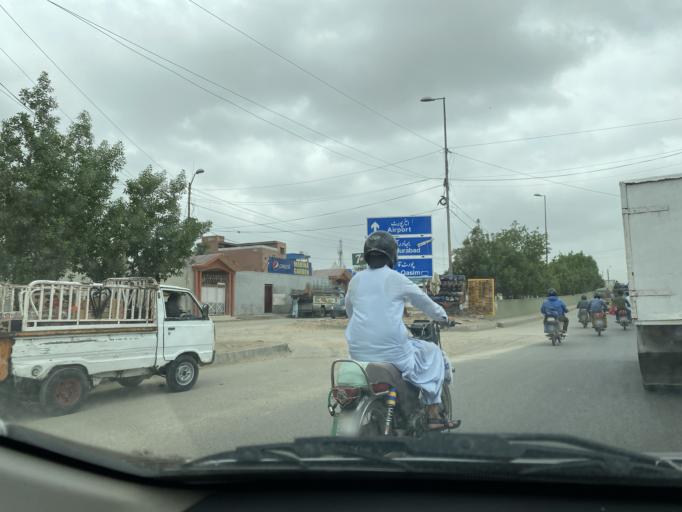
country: PK
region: Sindh
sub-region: Karachi District
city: Karachi
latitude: 24.8639
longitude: 67.0859
